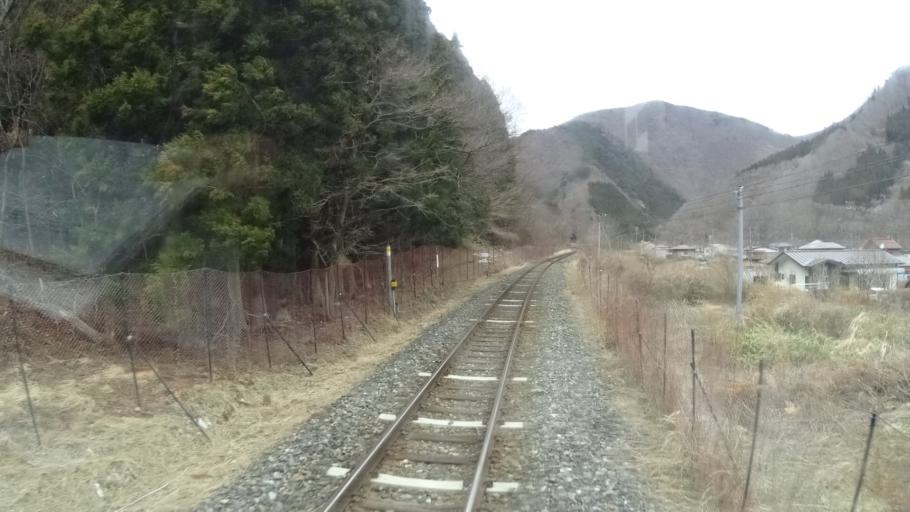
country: JP
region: Iwate
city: Kamaishi
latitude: 39.2523
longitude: 141.7533
